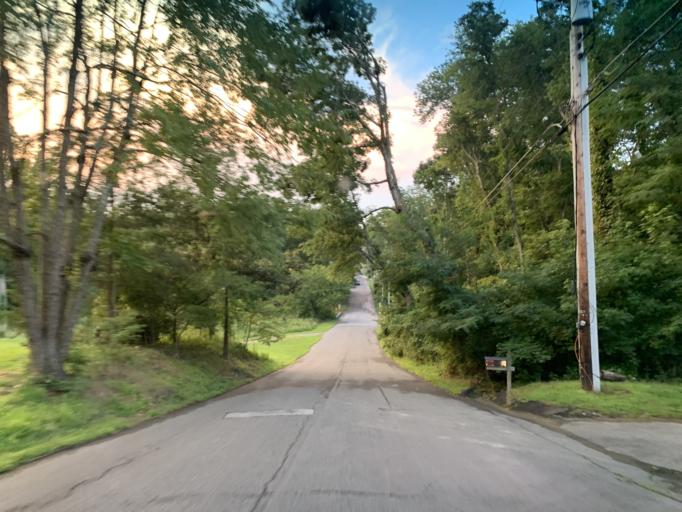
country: US
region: Maryland
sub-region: Harford County
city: Edgewood
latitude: 39.4156
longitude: -76.3369
